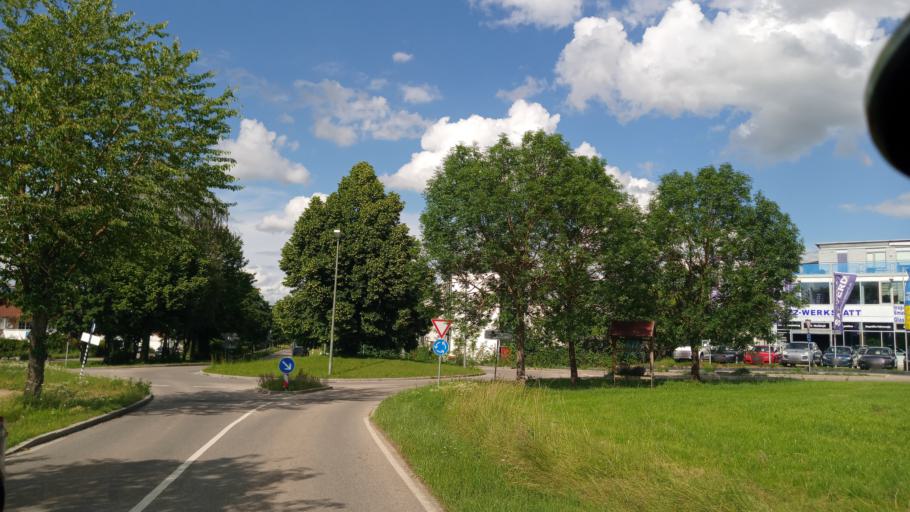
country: DE
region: Bavaria
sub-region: Upper Bavaria
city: Rohrmoos
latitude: 48.3573
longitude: 11.4389
